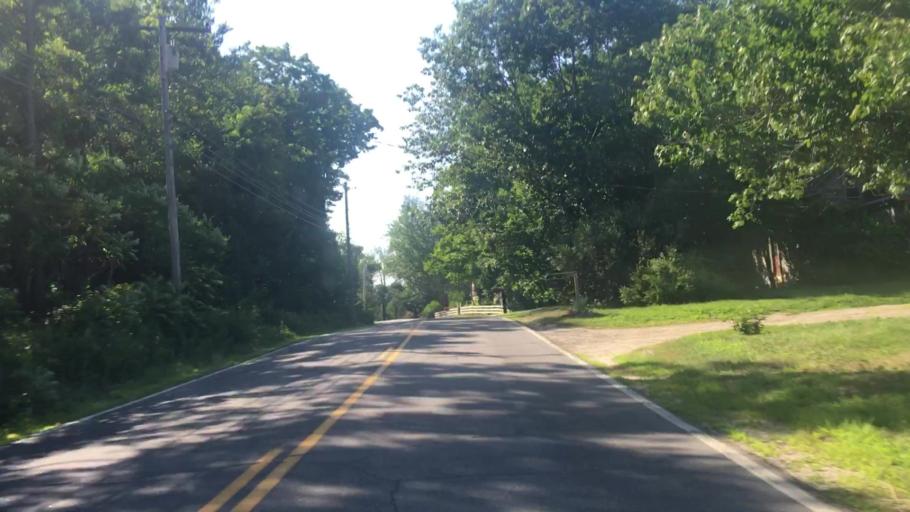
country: US
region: Maine
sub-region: York County
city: Hollis Center
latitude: 43.6401
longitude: -70.5821
